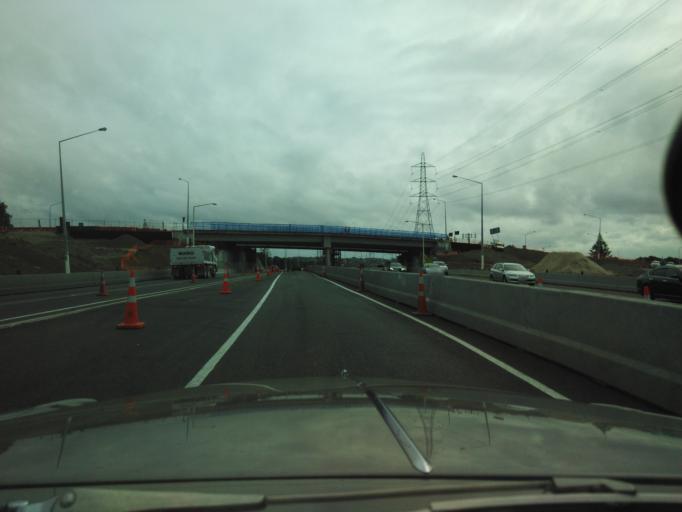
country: NZ
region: Auckland
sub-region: Auckland
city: Rosebank
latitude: -36.8580
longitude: 174.6536
